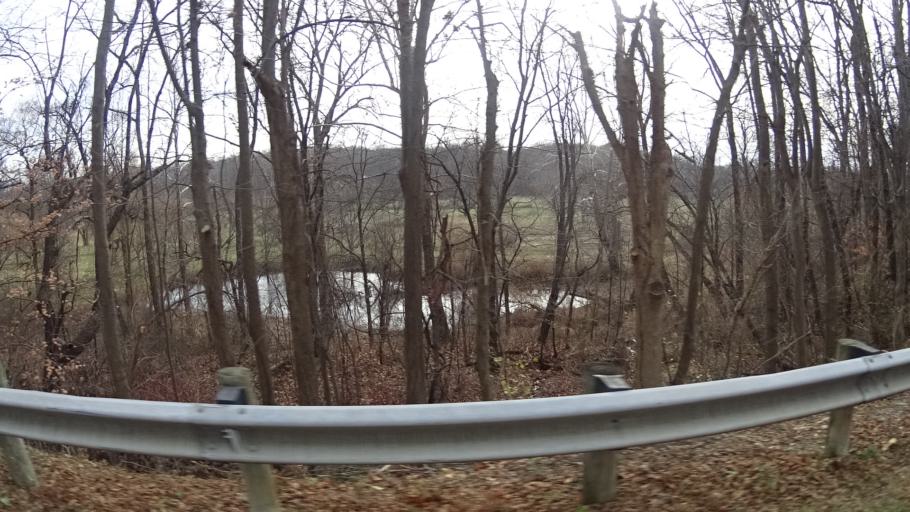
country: US
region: Ohio
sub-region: Lorain County
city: Eaton Estates
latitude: 41.2908
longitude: -81.9285
